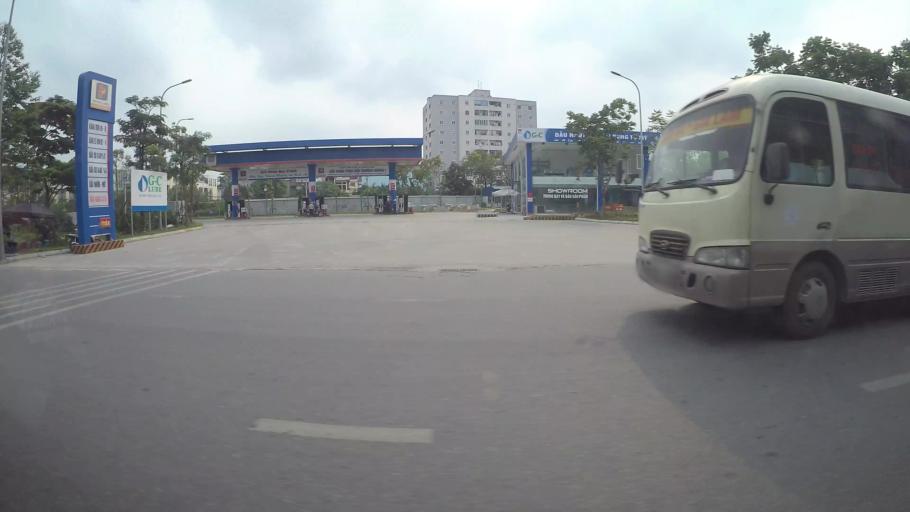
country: VN
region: Ha Noi
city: Hoan Kiem
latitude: 21.0537
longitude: 105.8891
